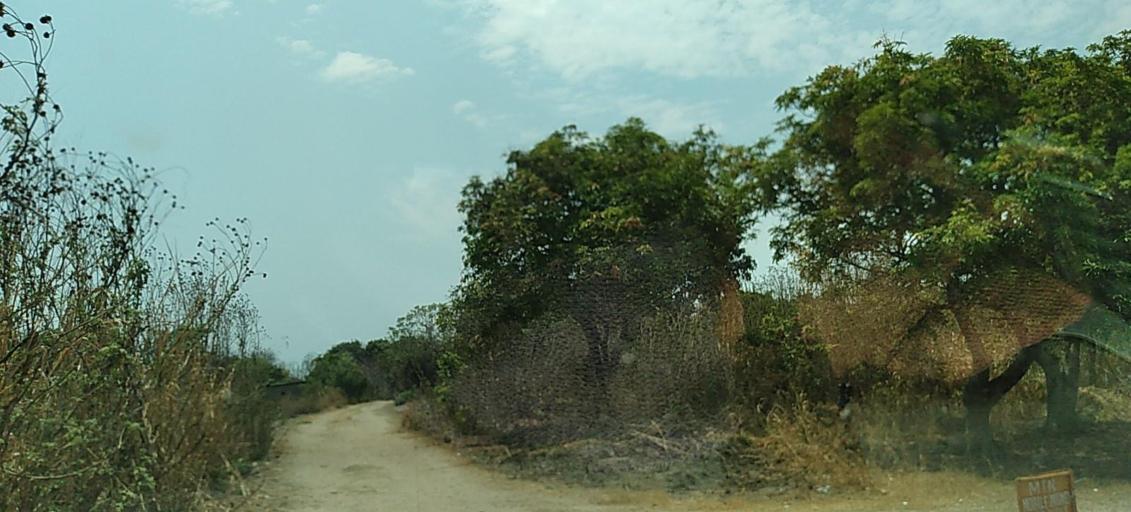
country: ZM
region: Copperbelt
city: Kalulushi
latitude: -12.9546
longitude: 28.1429
